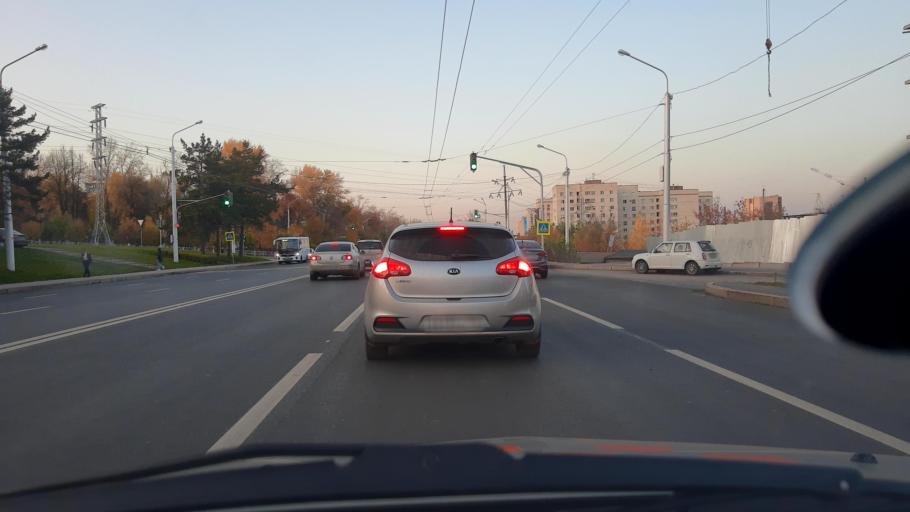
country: RU
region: Bashkortostan
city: Ufa
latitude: 54.7718
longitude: 56.0335
